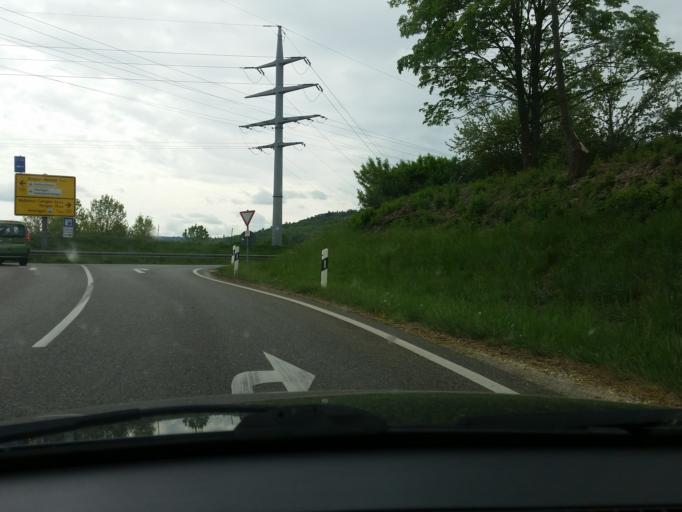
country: DE
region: Baden-Wuerttemberg
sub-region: Freiburg Region
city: Hilzingen
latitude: 47.7628
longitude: 8.7963
